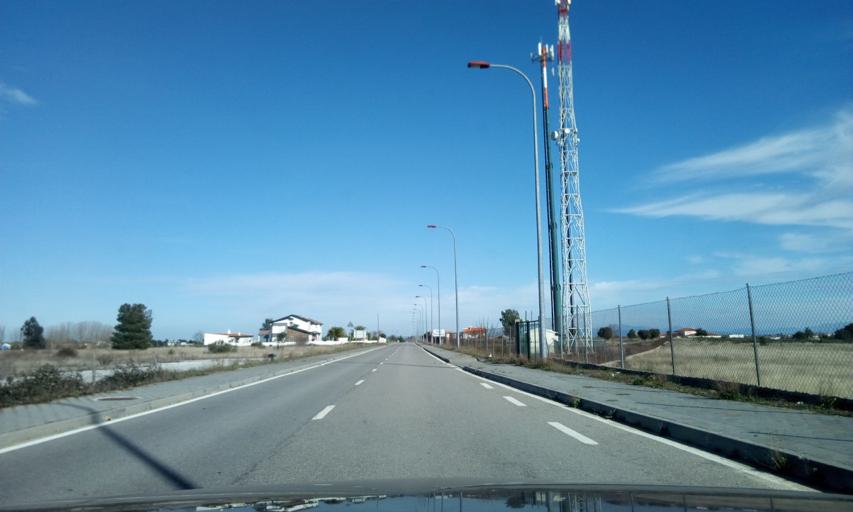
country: ES
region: Castille and Leon
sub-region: Provincia de Salamanca
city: Fuentes de Onoro
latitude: 40.6172
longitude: -6.8529
